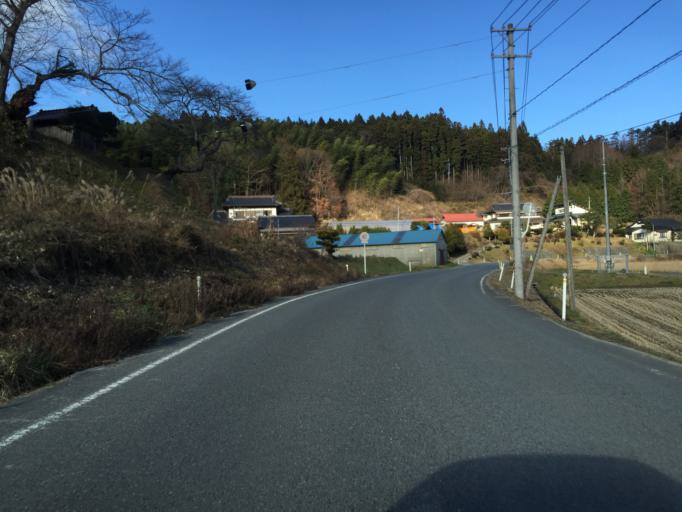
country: JP
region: Fukushima
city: Ishikawa
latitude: 37.2402
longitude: 140.6208
